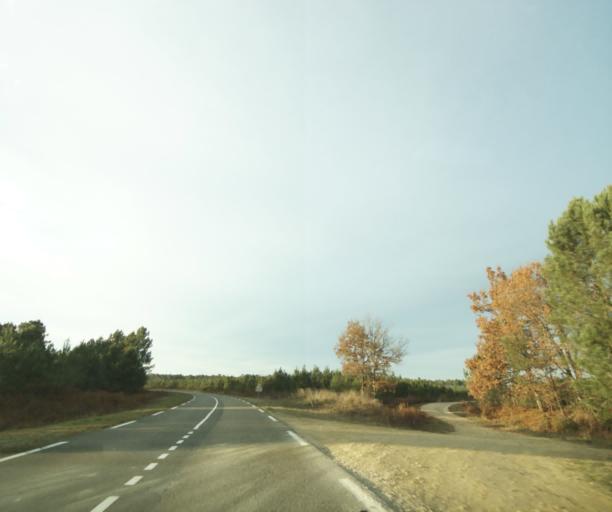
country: FR
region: Aquitaine
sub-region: Departement des Landes
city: Gabarret
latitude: 44.0856
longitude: -0.0753
